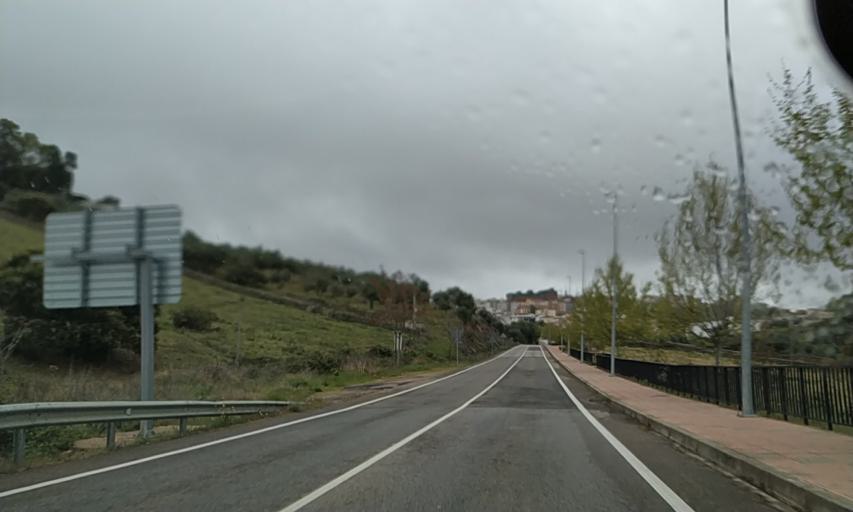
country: ES
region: Extremadura
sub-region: Provincia de Caceres
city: Caceres
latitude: 39.4849
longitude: -6.3818
